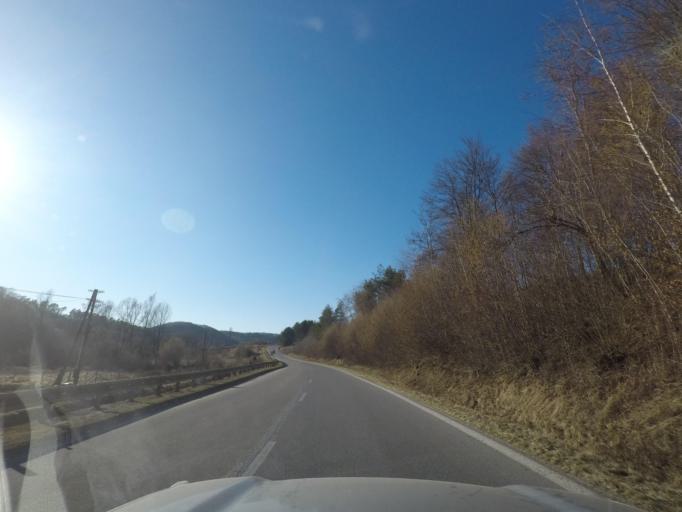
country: SK
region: Presovsky
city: Medzilaborce
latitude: 49.2492
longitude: 21.9269
